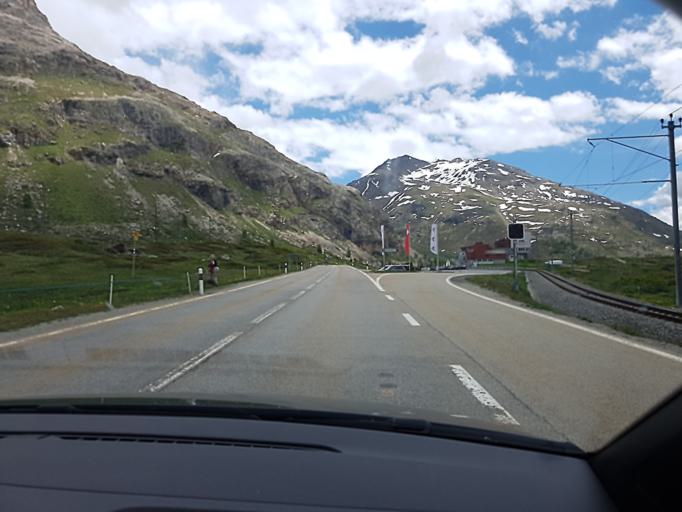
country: CH
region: Grisons
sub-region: Maloja District
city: Pontresina
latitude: 46.4428
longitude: 9.9792
